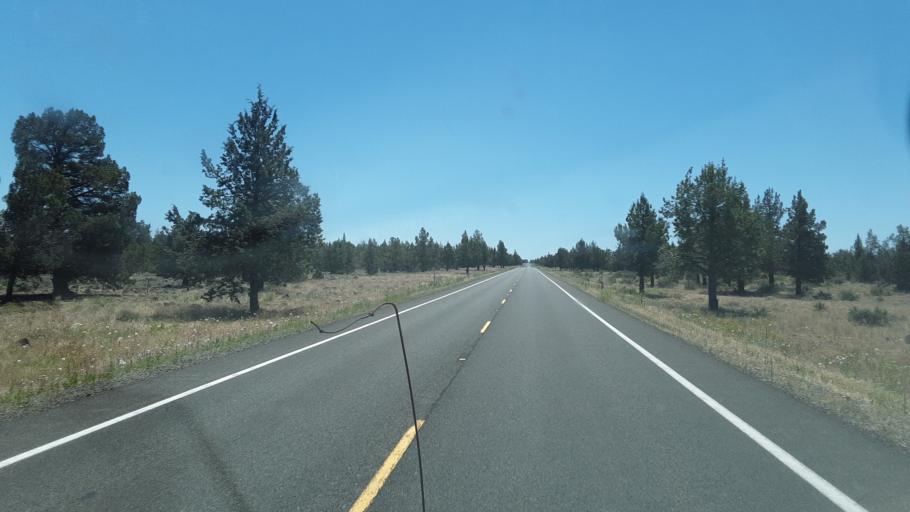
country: US
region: California
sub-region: Siskiyou County
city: Tulelake
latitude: 41.6610
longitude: -121.2499
